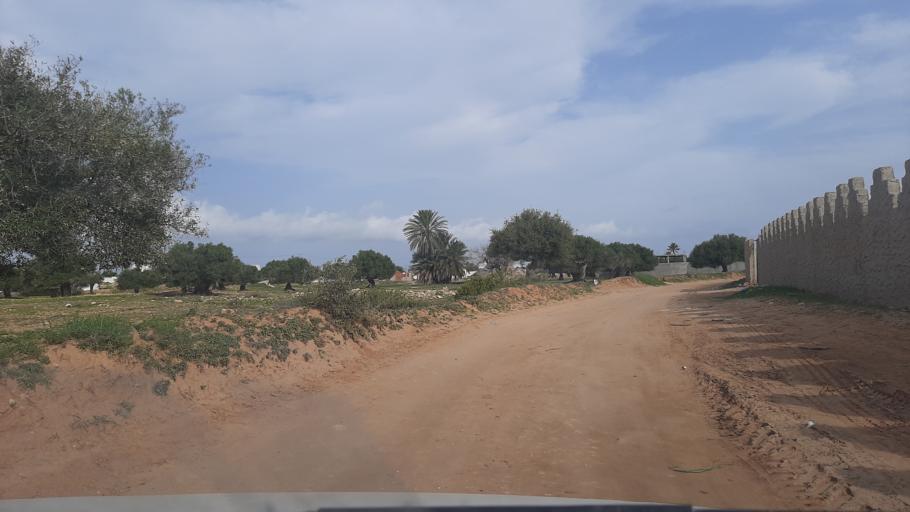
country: TN
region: Madanin
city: Midoun
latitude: 33.8077
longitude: 11.0236
